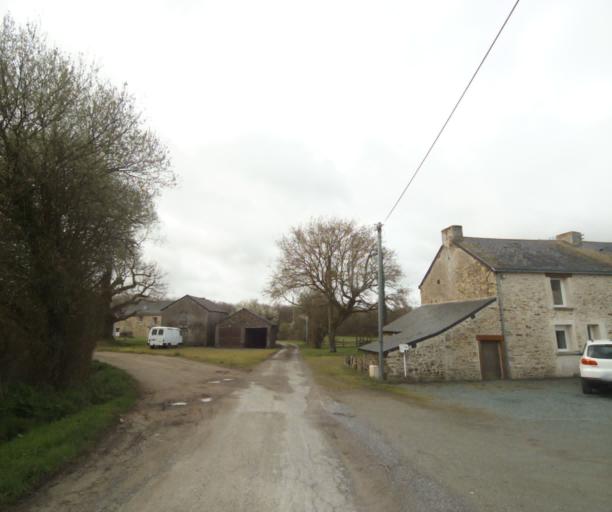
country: FR
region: Pays de la Loire
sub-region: Departement de la Loire-Atlantique
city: Bouvron
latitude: 47.4035
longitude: -1.8903
